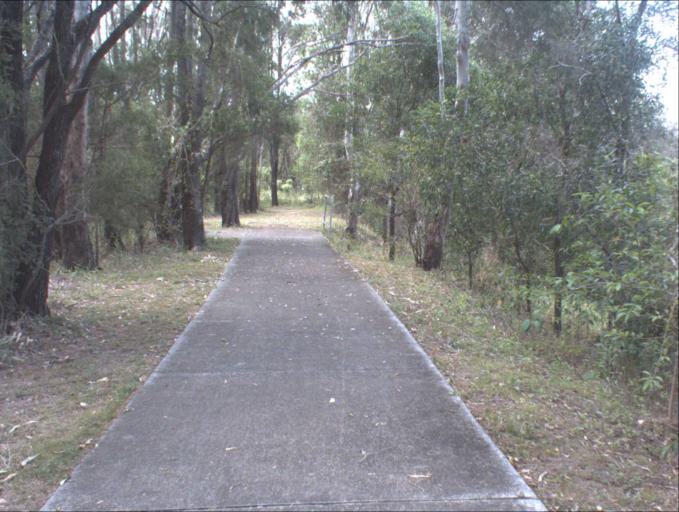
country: AU
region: Queensland
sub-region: Logan
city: Slacks Creek
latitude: -27.6688
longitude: 153.1593
